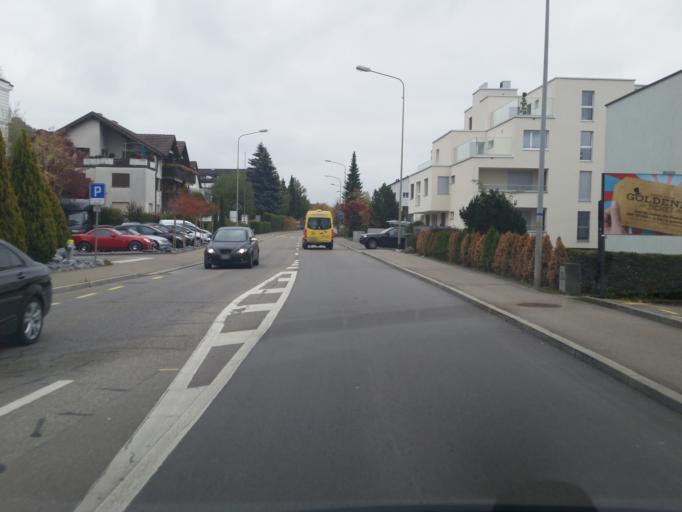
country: CH
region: Zurich
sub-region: Bezirk Dietikon
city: Geroldswil
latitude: 47.4209
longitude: 8.4097
